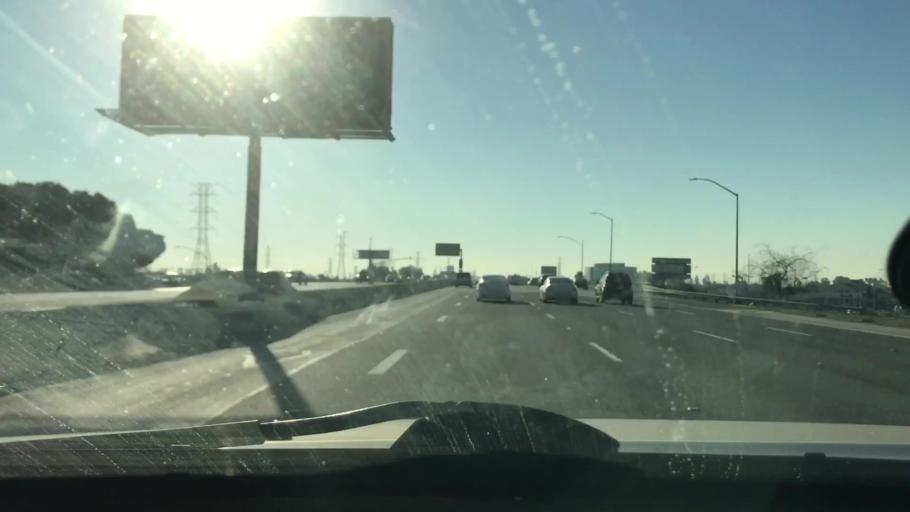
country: US
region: California
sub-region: Los Angeles County
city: Carson
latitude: 33.8400
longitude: -118.2646
